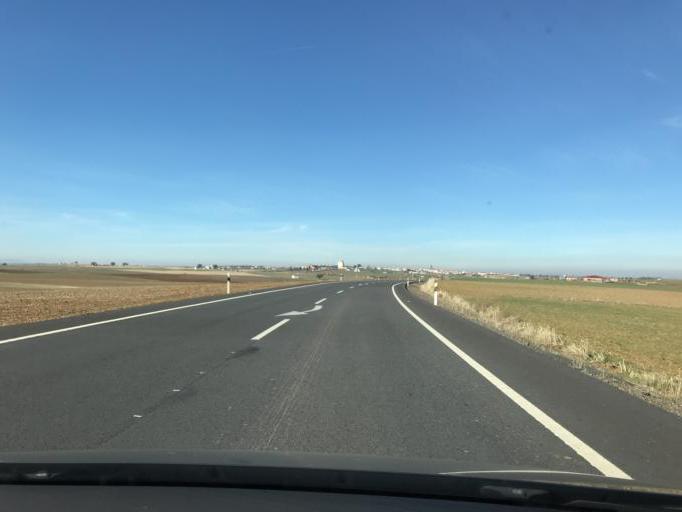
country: ES
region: Extremadura
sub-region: Provincia de Badajoz
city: Granja de Torrehermosa
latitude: 38.2991
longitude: -5.5639
